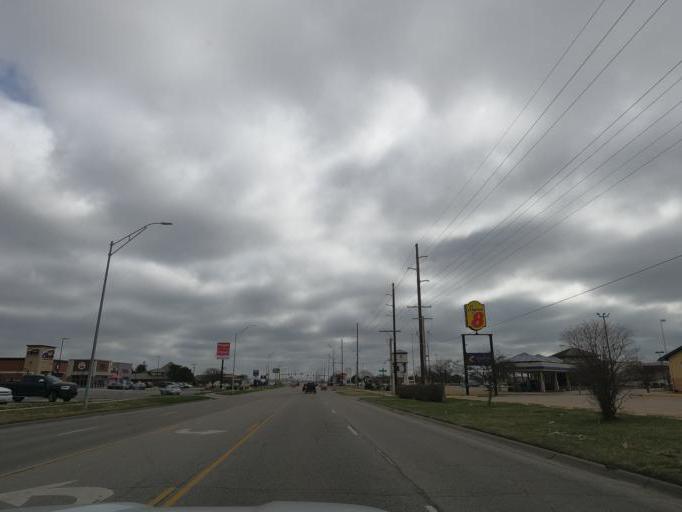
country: US
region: Kansas
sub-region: Reno County
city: Hutchinson
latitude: 38.0722
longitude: -97.9007
